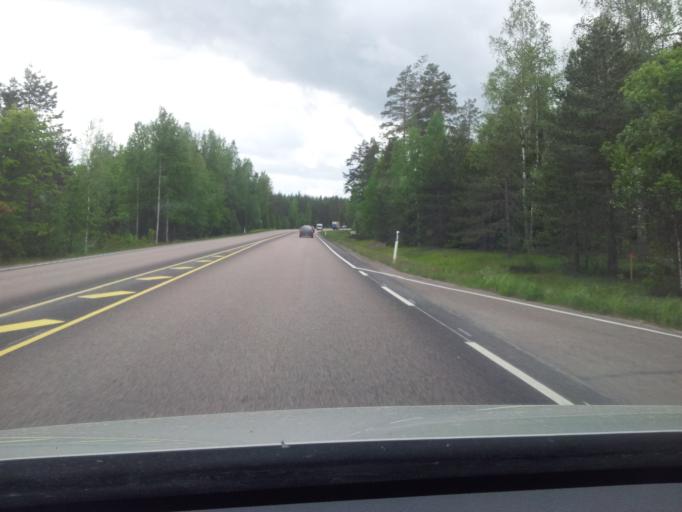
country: FI
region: South Karelia
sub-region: Lappeenranta
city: Taavetti
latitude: 60.9145
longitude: 27.4006
